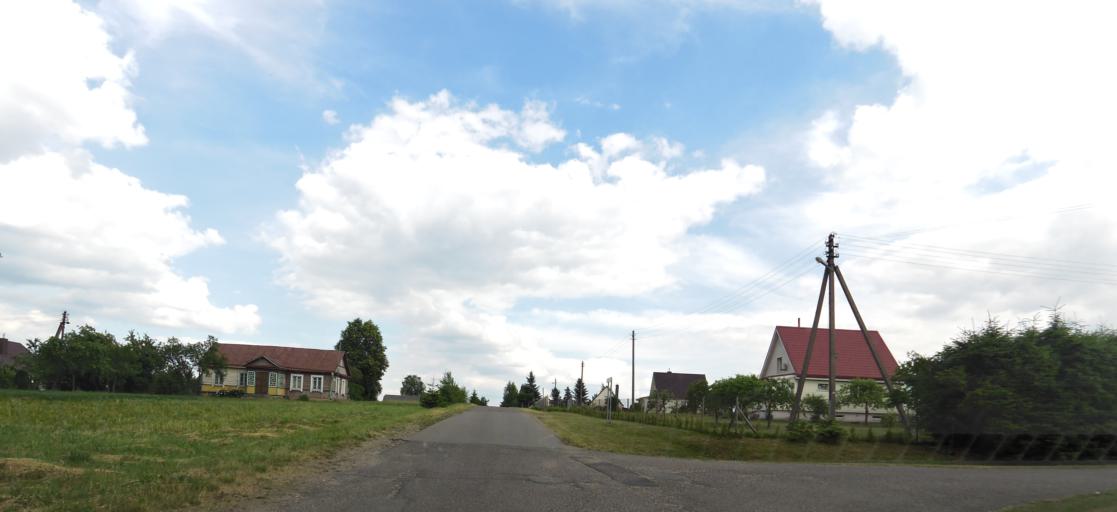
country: LT
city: Skaidiskes
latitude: 54.5334
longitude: 25.6430
